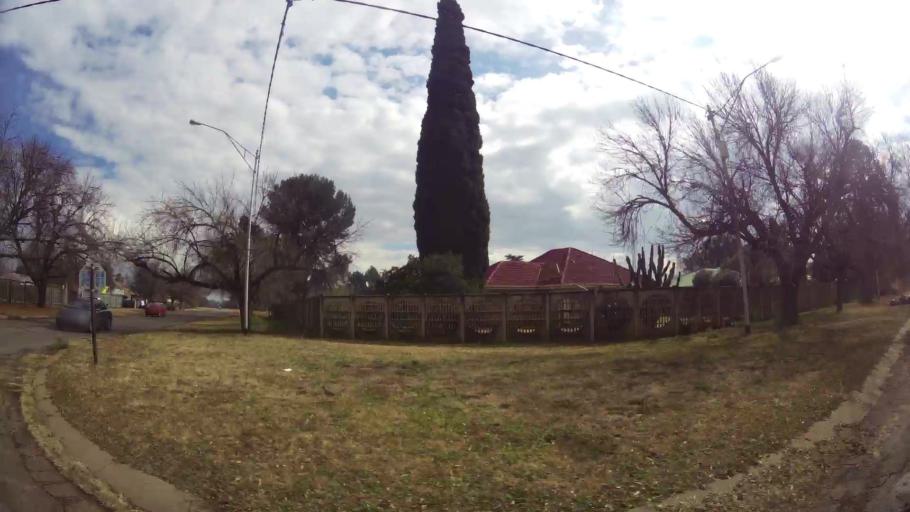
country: ZA
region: Gauteng
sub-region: Sedibeng District Municipality
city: Vereeniging
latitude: -26.6516
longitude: 27.9699
